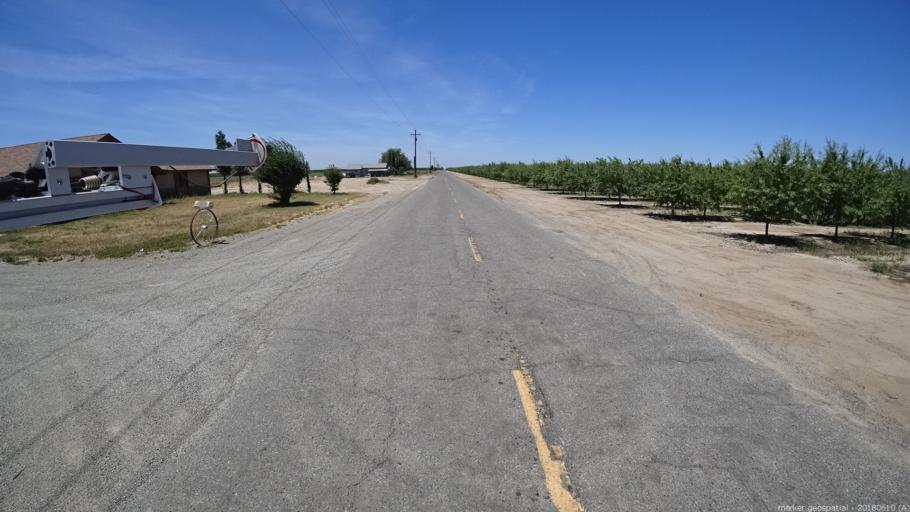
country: US
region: California
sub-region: Madera County
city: Chowchilla
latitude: 37.0543
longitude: -120.3741
